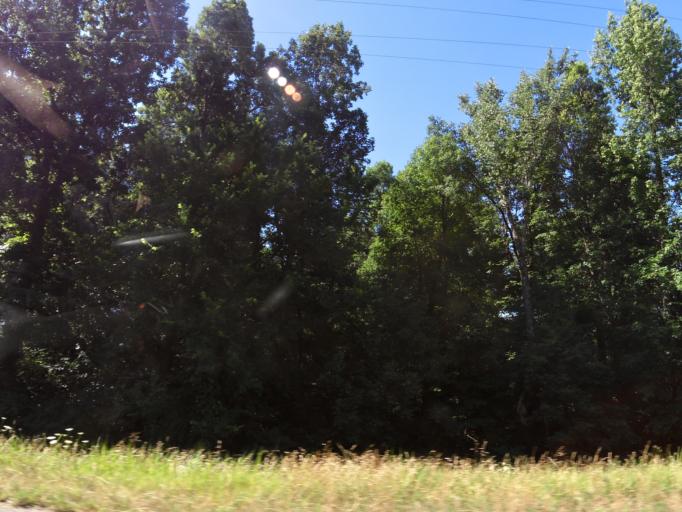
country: US
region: Arkansas
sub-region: Clay County
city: Piggott
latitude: 36.4327
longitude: -90.3069
